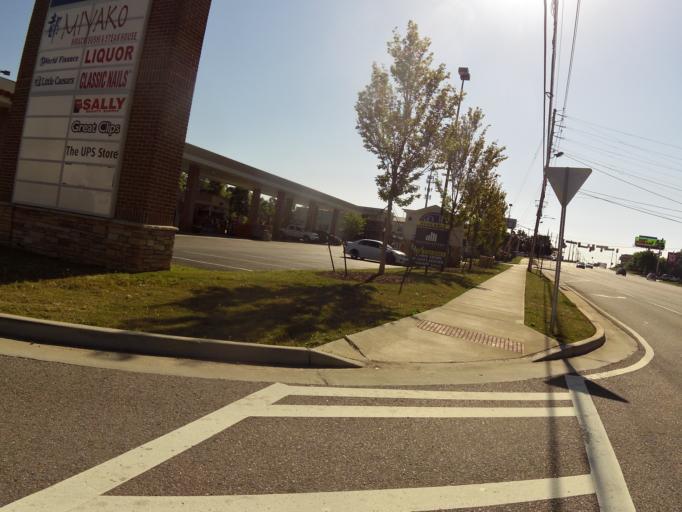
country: US
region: Georgia
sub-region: Columbia County
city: Martinez
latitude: 33.5104
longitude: -82.0299
